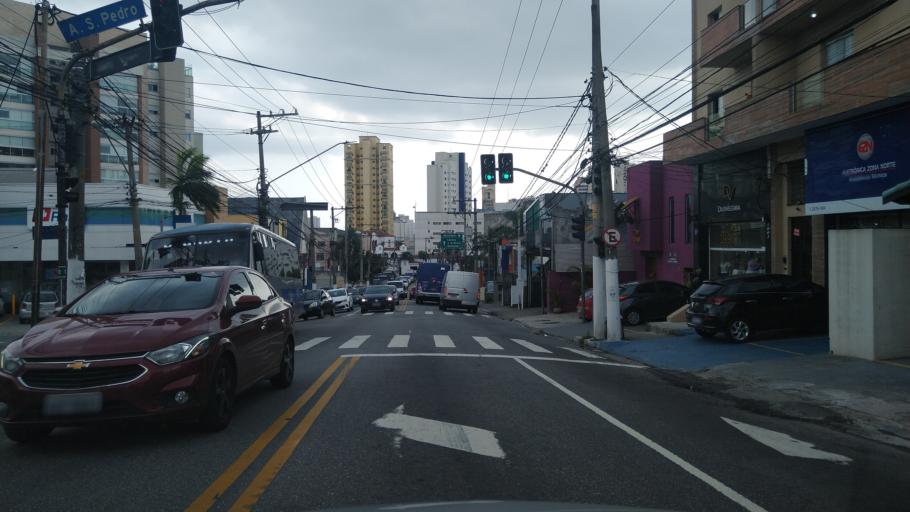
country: BR
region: Sao Paulo
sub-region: Sao Paulo
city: Sao Paulo
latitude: -23.4855
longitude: -46.6162
